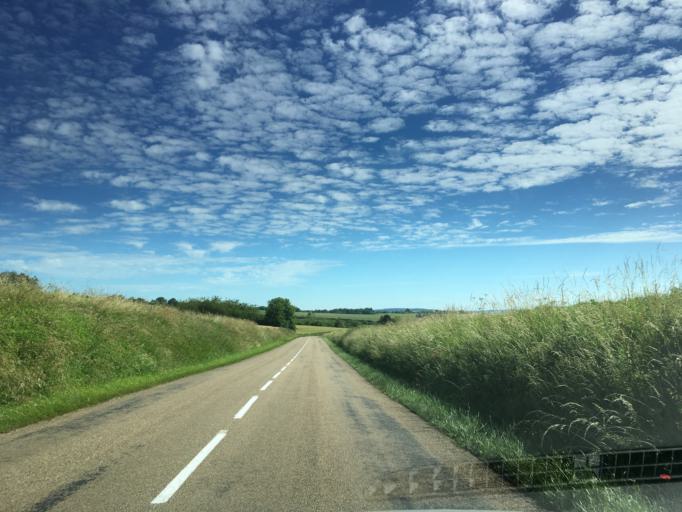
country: FR
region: Bourgogne
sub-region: Departement de l'Yonne
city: Saint-Georges-sur-Baulche
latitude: 47.7710
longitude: 3.5329
